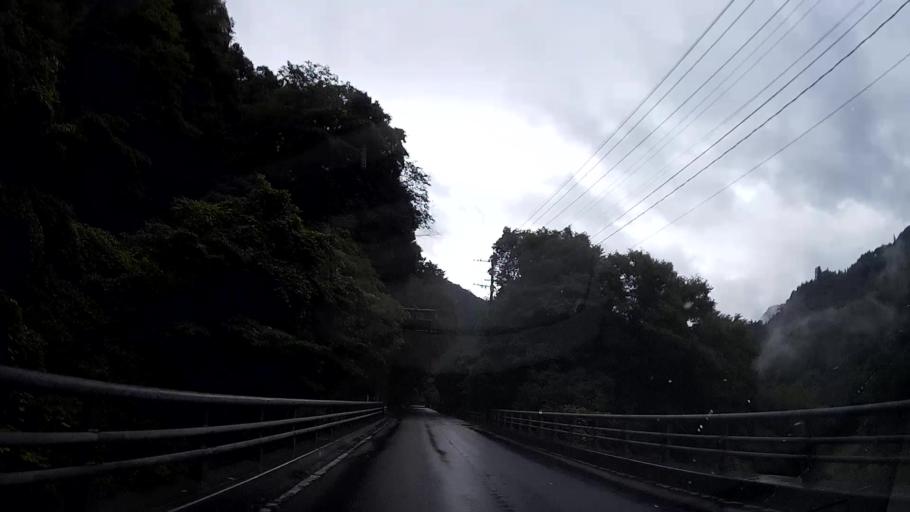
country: JP
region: Oita
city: Hita
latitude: 33.1810
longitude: 131.0042
